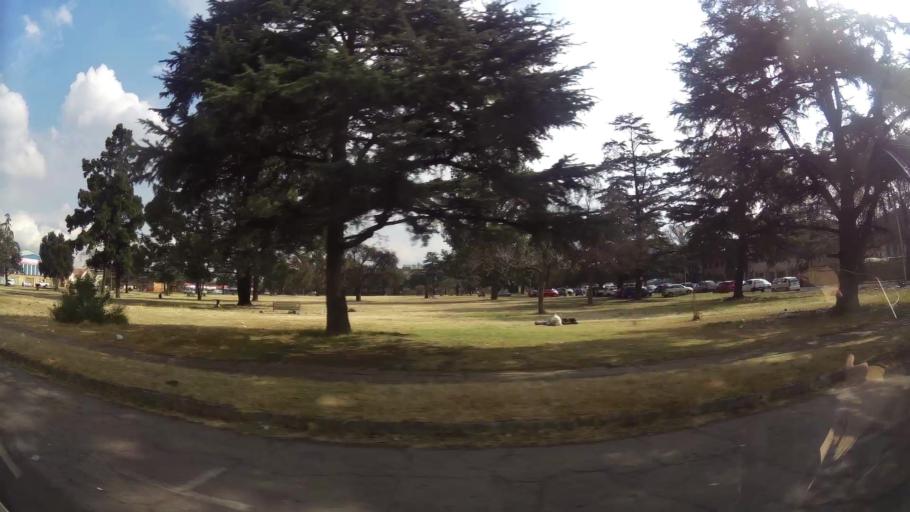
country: ZA
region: Gauteng
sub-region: Sedibeng District Municipality
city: Vereeniging
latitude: -26.6820
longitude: 27.9299
